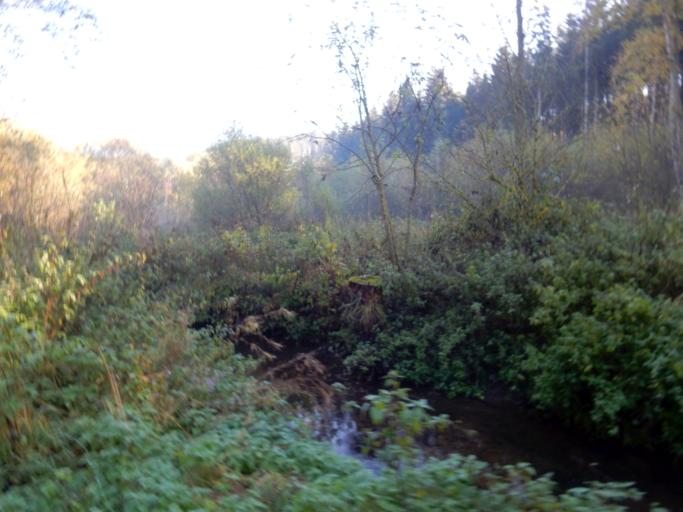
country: LU
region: Diekirch
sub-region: Canton de Clervaux
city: Troisvierges
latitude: 50.1241
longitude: 5.9861
